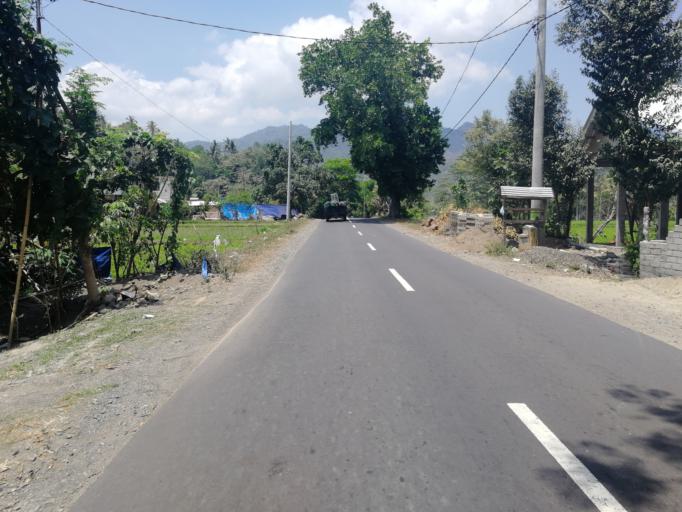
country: ID
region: West Nusa Tenggara
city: Karangsubagan
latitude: -8.4352
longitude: 116.0876
